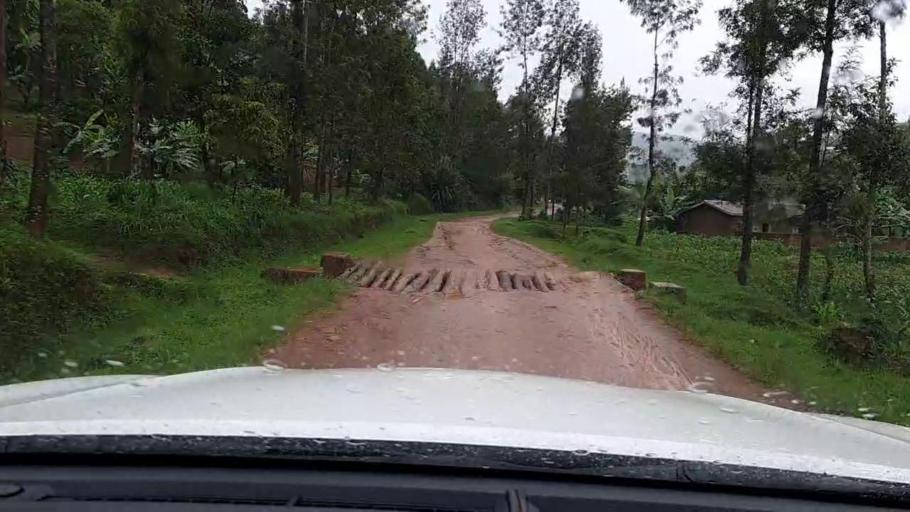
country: RW
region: Northern Province
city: Byumba
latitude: -1.7292
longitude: 29.9358
